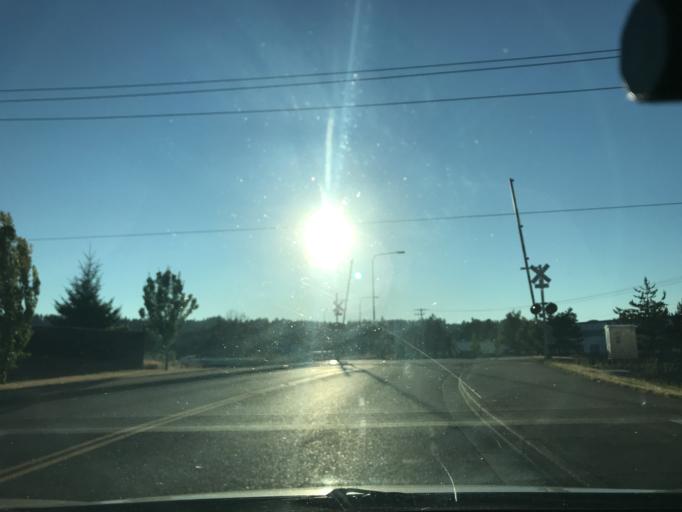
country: US
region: Washington
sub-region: Pierce County
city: Sumner
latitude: 47.2125
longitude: -122.2311
